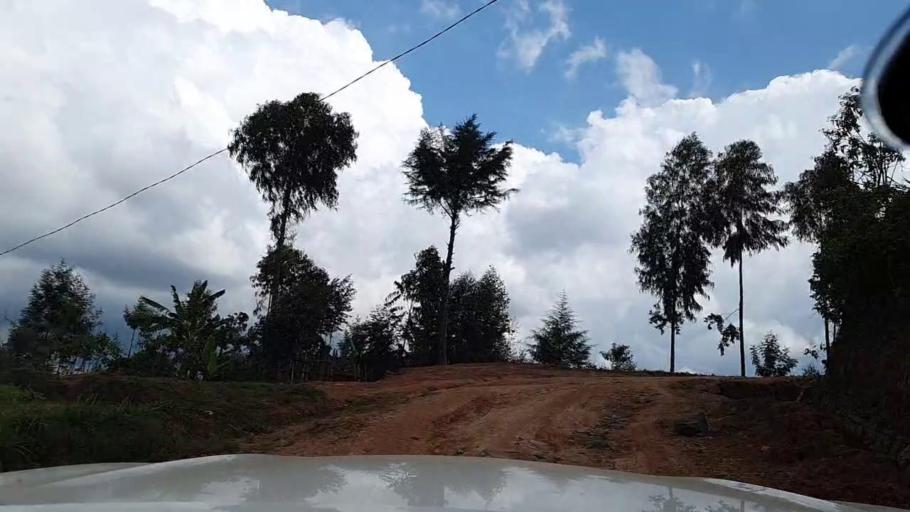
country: RW
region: Southern Province
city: Nzega
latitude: -2.7036
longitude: 29.4335
